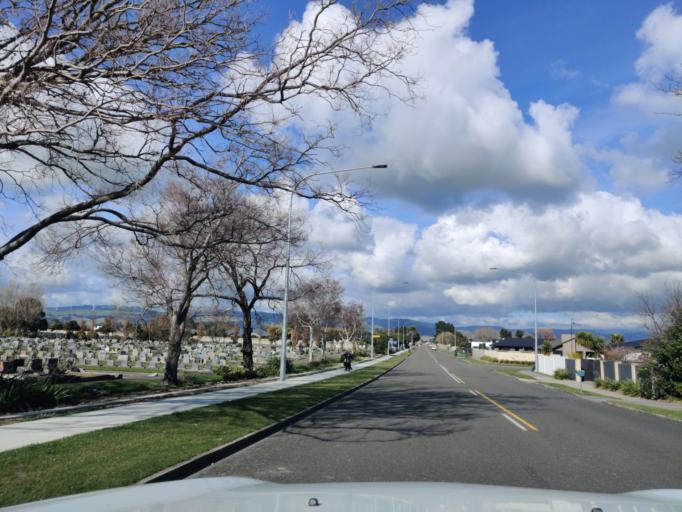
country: NZ
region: Manawatu-Wanganui
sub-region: Palmerston North City
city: Palmerston North
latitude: -40.3243
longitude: 175.6611
